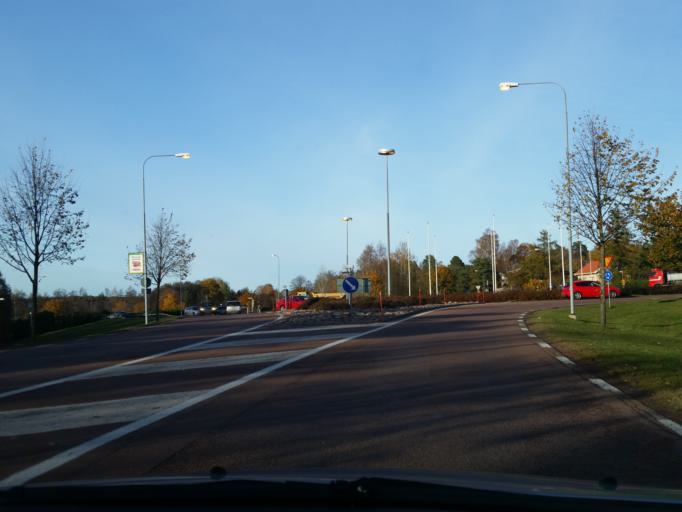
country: AX
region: Mariehamns stad
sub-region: Mariehamn
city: Mariehamn
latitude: 60.1128
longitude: 19.9294
